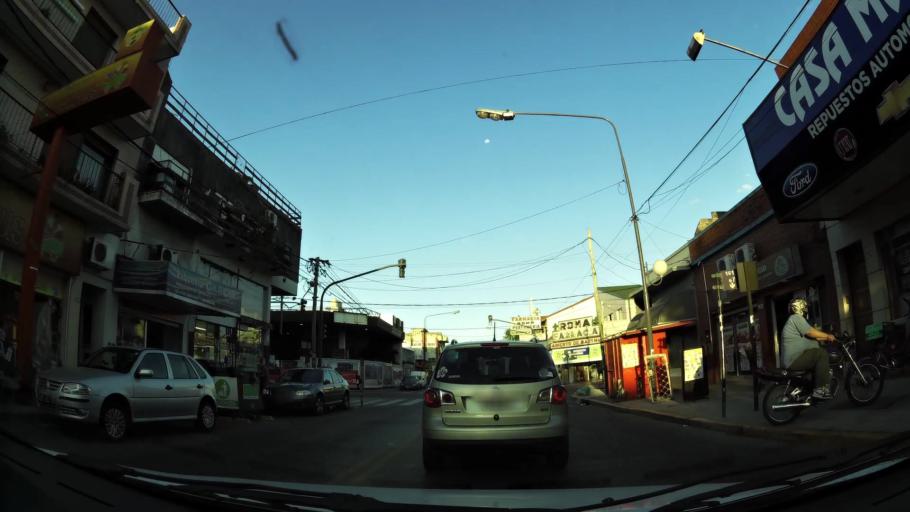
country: AR
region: Buenos Aires
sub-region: Partido de General San Martin
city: General San Martin
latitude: -34.5472
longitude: -58.5026
